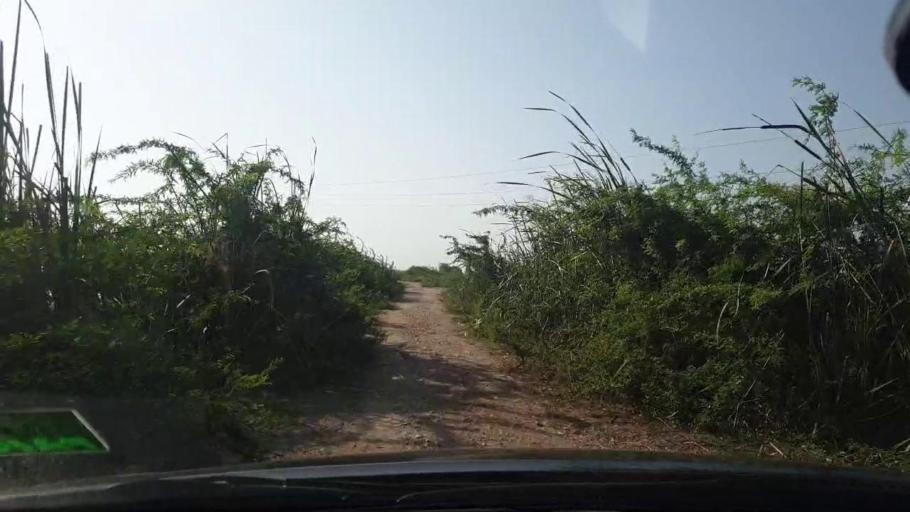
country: PK
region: Sindh
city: Tando Bago
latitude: 24.7095
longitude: 68.9545
